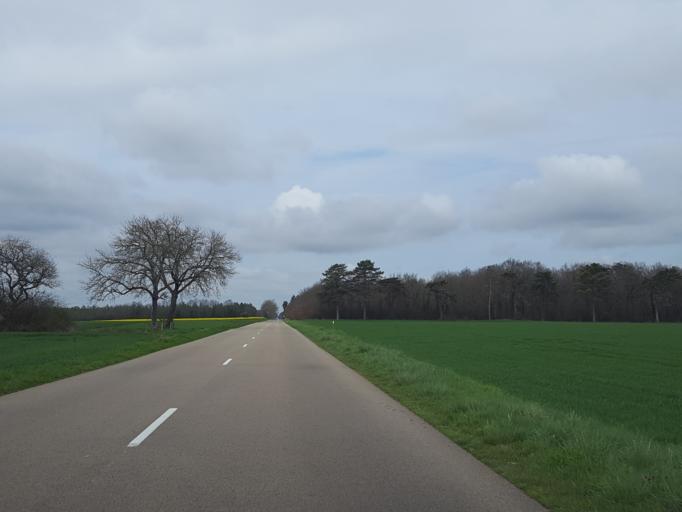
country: FR
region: Centre
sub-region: Departement du Loiret
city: Sainte-Genevieve-des-Bois
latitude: 47.8291
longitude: 2.7955
